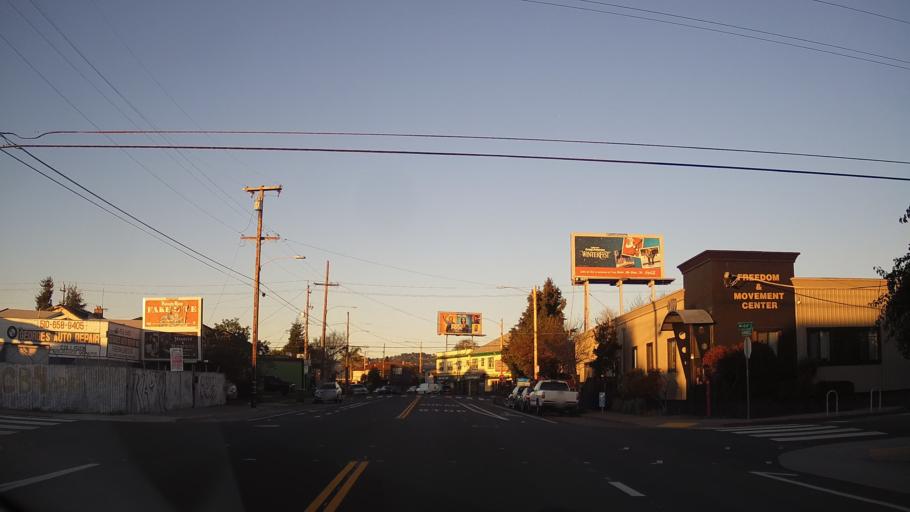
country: US
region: California
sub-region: Alameda County
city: Emeryville
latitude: 37.8336
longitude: -122.2732
